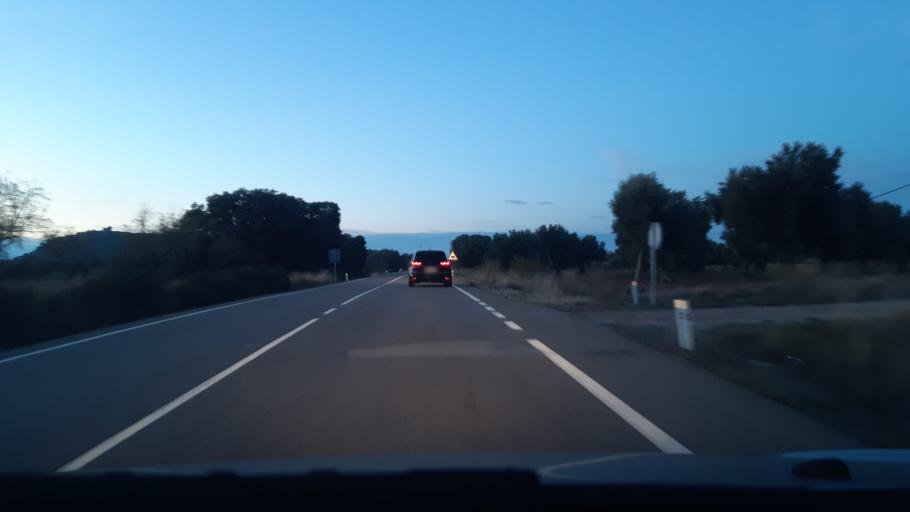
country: ES
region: Aragon
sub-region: Provincia de Teruel
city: Calaceite
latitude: 40.9957
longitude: 0.1968
